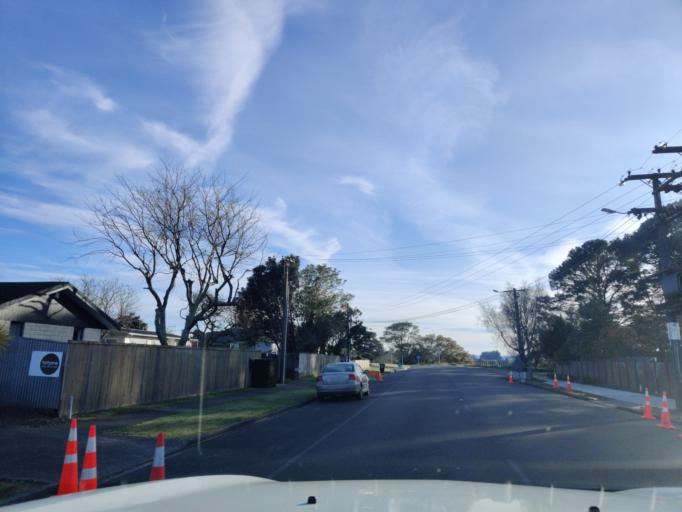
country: NZ
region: Manawatu-Wanganui
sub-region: Palmerston North City
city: Palmerston North
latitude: -40.2825
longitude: 175.7603
